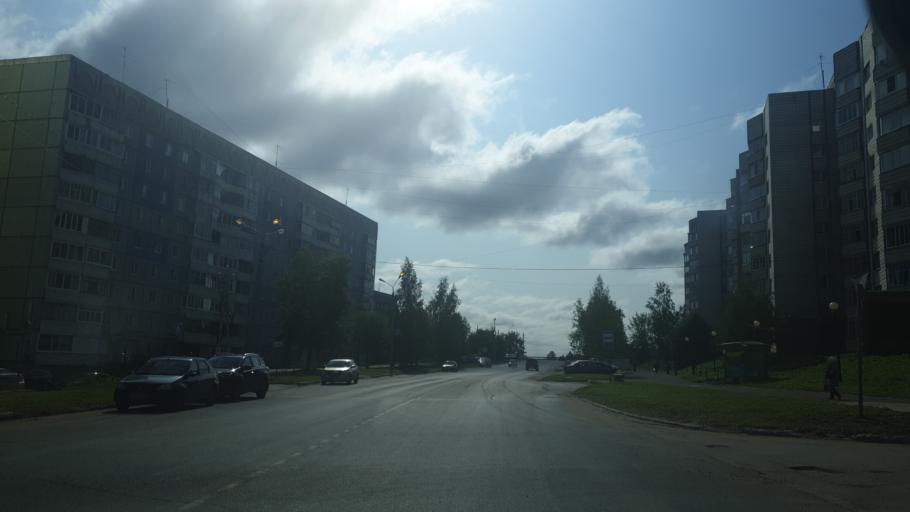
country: RU
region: Komi Republic
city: Ezhva
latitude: 61.7851
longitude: 50.7578
